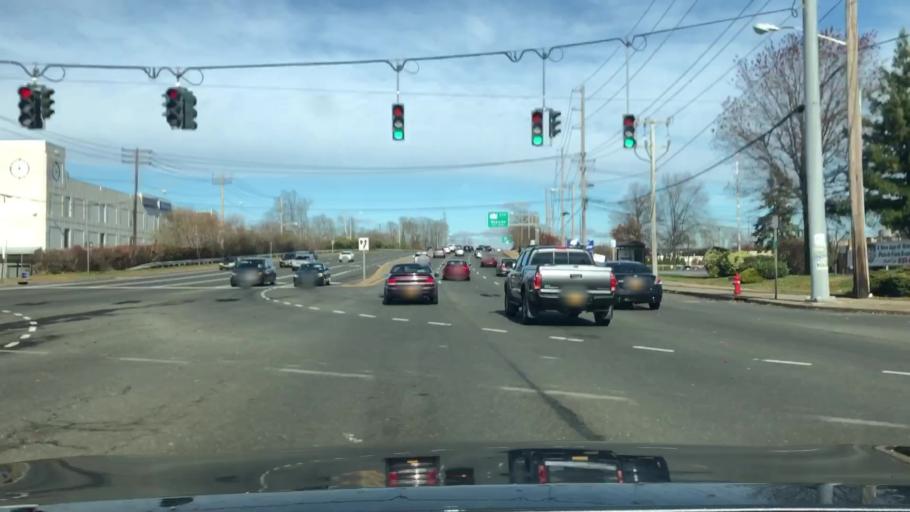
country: US
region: New York
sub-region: Nassau County
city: South Farmingdale
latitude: 40.7185
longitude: -73.4261
